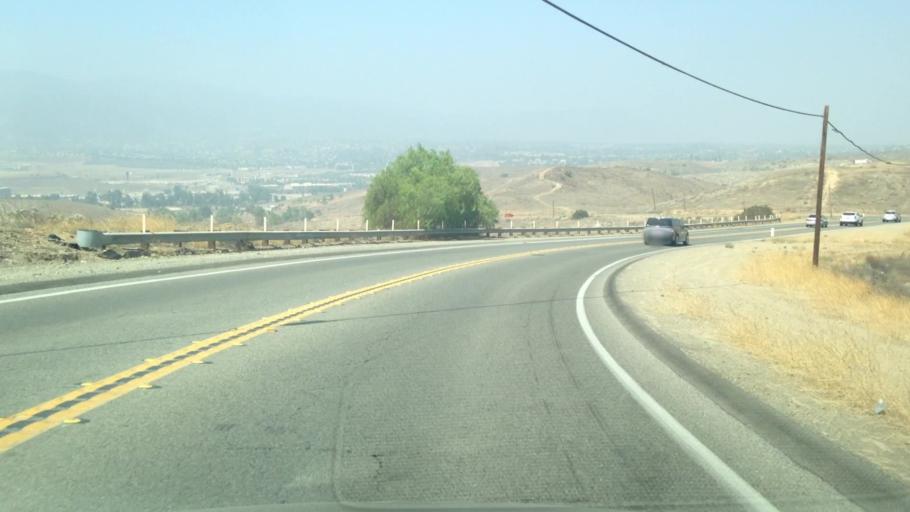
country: US
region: California
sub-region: Riverside County
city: El Cerrito
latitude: 33.8274
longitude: -117.4854
